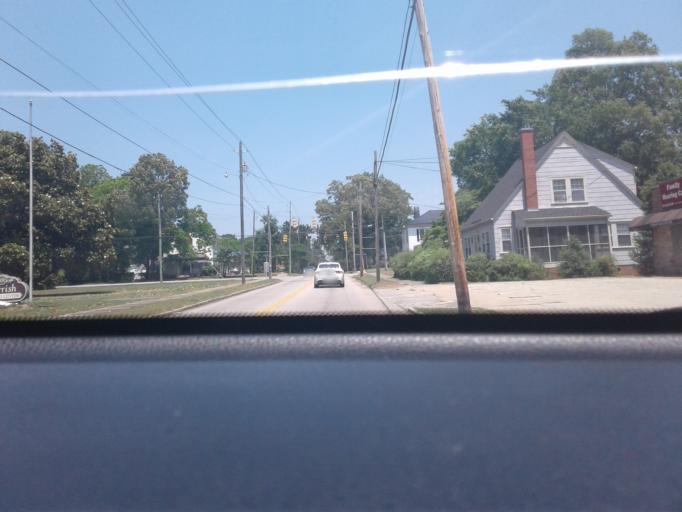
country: US
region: North Carolina
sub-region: Harnett County
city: Dunn
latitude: 35.3122
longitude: -78.6146
